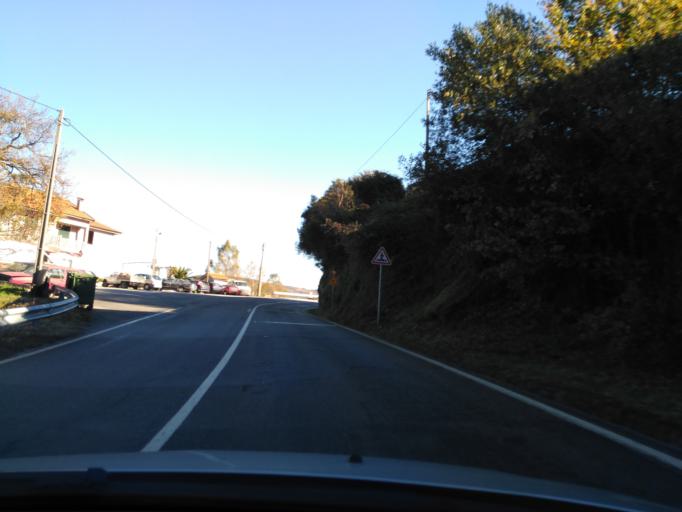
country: PT
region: Braga
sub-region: Vieira do Minho
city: Vieira do Minho
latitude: 41.6807
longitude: -8.0241
